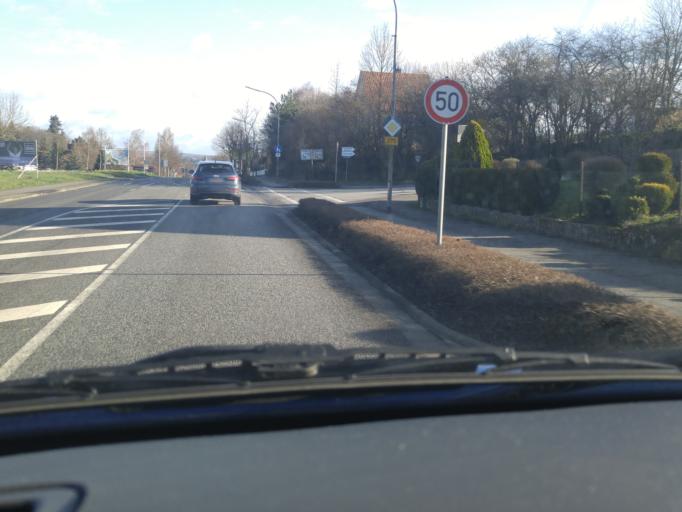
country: DE
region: Hesse
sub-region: Regierungsbezirk Giessen
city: Lauterbach
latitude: 50.6250
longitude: 9.3939
